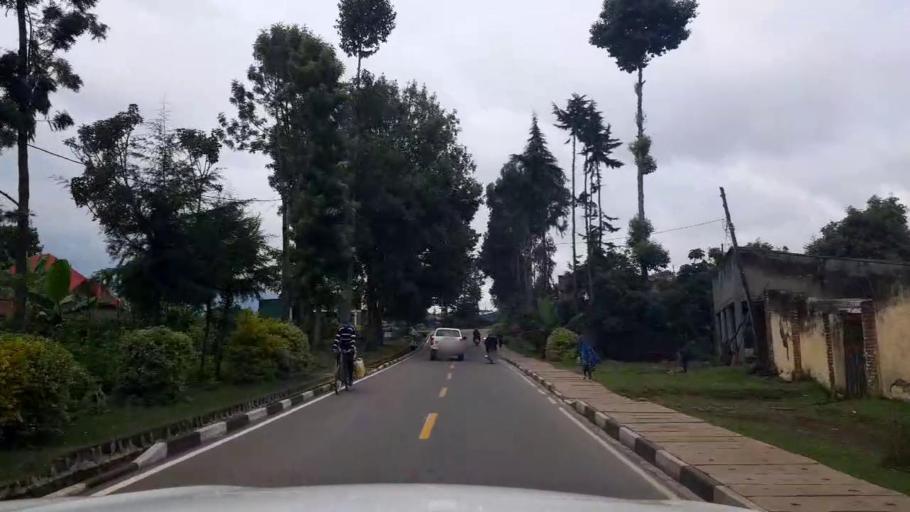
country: RW
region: Northern Province
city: Musanze
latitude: -1.4500
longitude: 29.5917
